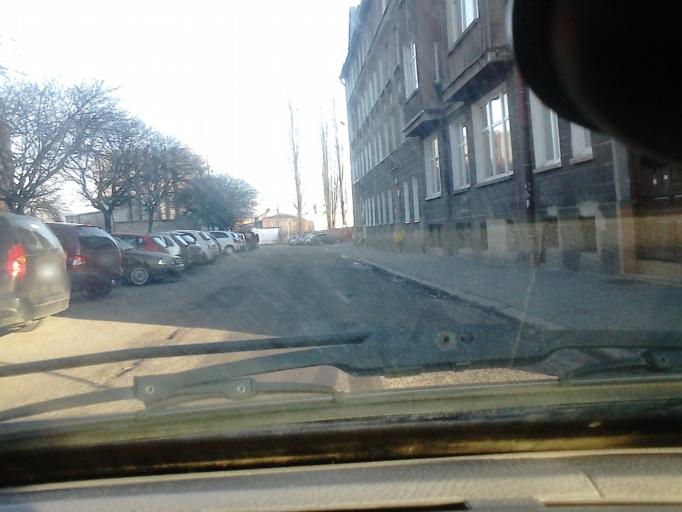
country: PL
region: Pomeranian Voivodeship
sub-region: Gdansk
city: Gdansk
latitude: 54.3585
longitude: 18.6548
